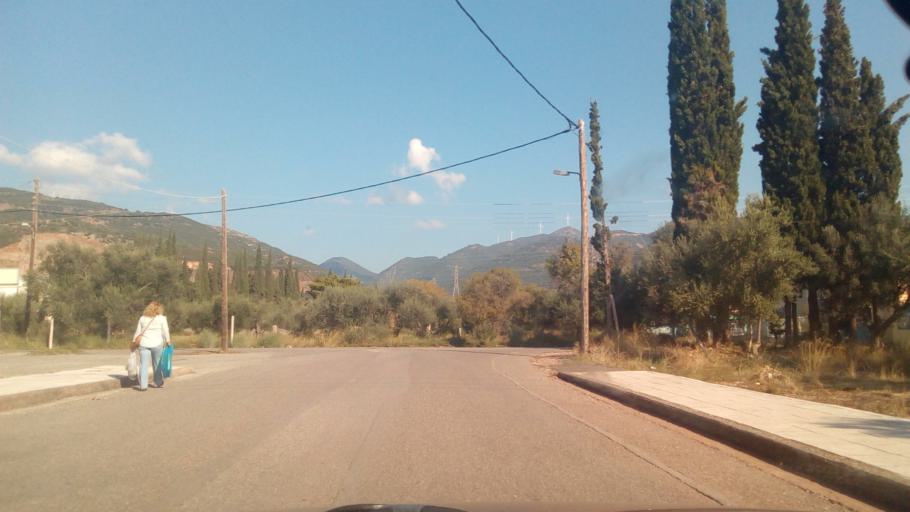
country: GR
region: West Greece
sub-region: Nomos Aitolias kai Akarnanias
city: Nafpaktos
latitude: 38.4007
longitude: 21.8456
